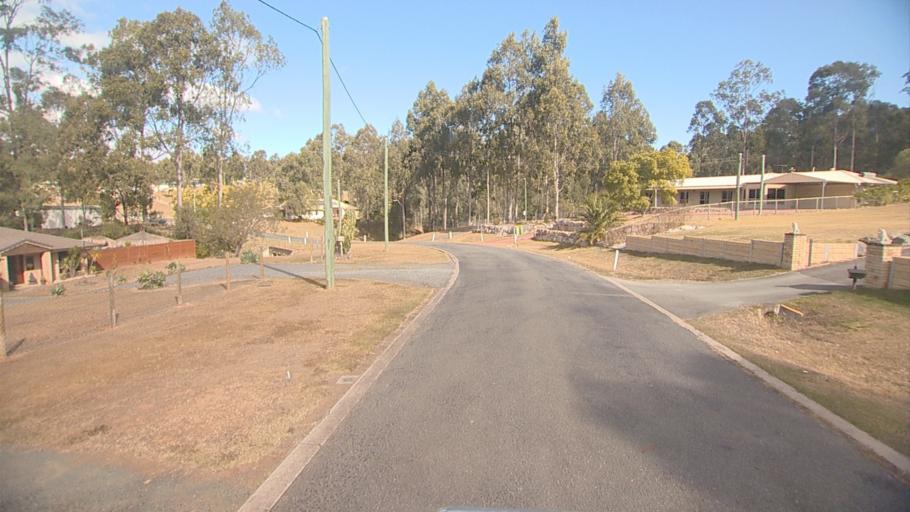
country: AU
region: Queensland
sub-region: Logan
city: Cedar Vale
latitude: -27.8722
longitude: 152.9985
